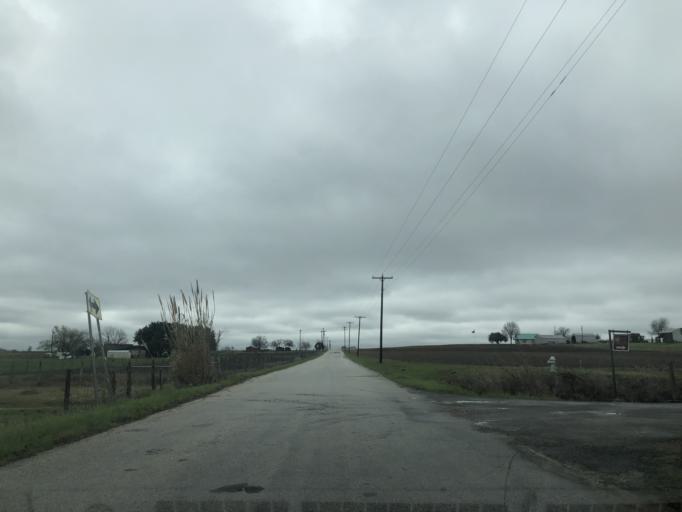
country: US
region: Texas
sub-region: Williamson County
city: Hutto
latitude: 30.5839
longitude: -97.4974
